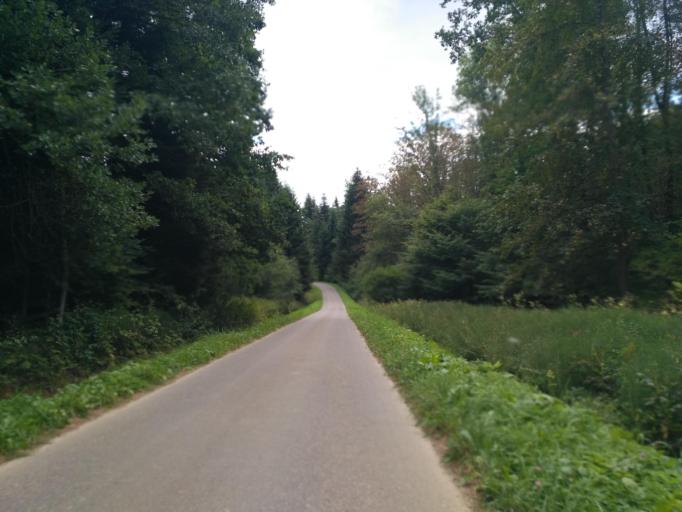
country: PL
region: Subcarpathian Voivodeship
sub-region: Powiat rzeszowski
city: Dynow
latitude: 49.7645
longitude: 22.2741
